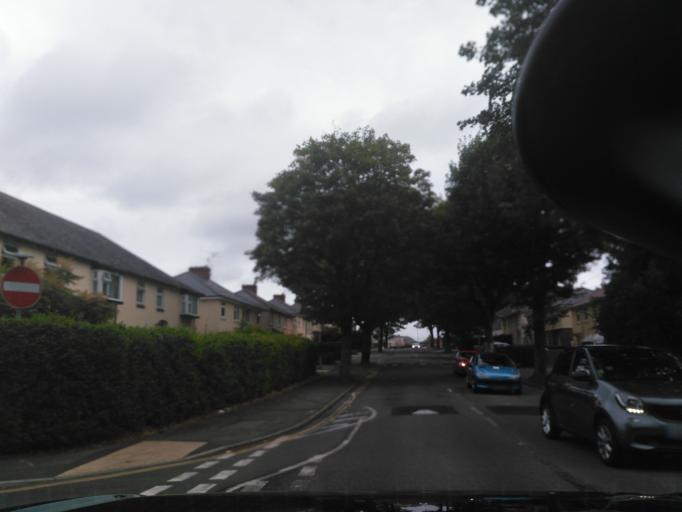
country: GB
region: England
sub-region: Borough of Swindon
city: Swindon
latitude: 51.5807
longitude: -1.7827
